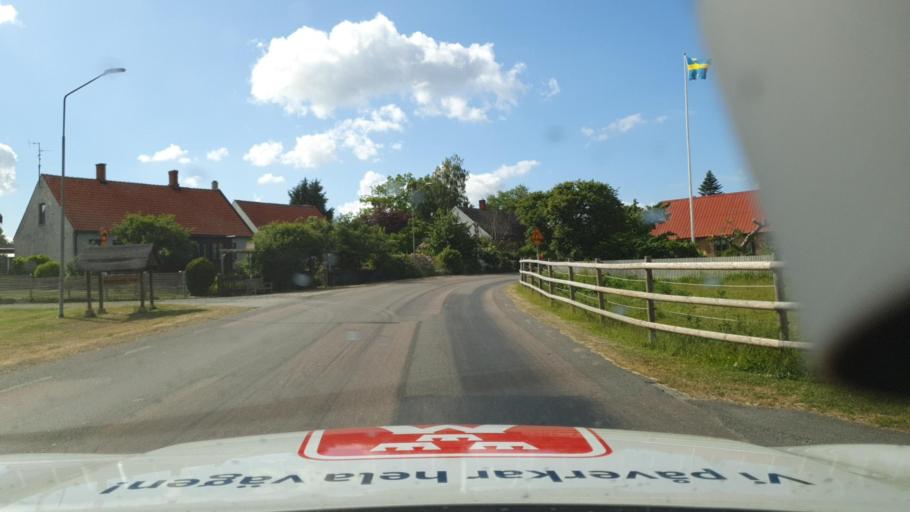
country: SE
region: Skane
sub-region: Simrishamns Kommun
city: Simrishamn
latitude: 55.5537
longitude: 14.3152
